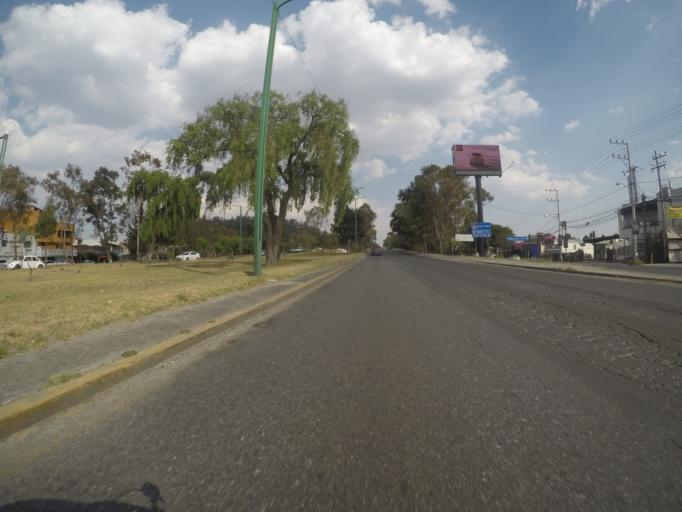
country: MX
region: Morelos
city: Metepec
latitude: 19.2493
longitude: -99.6119
